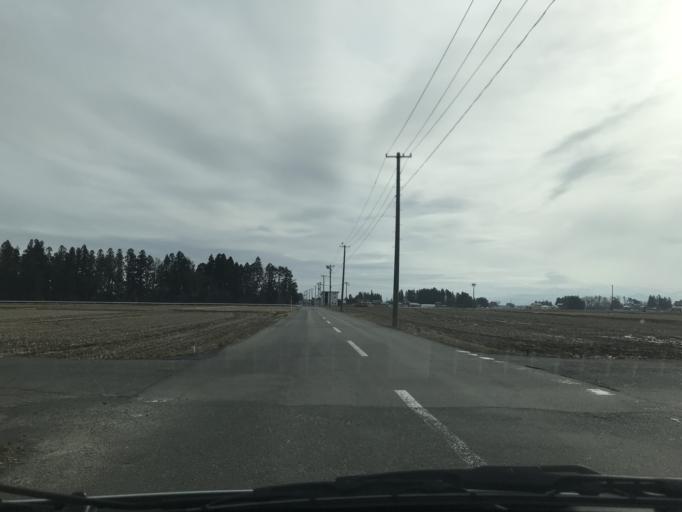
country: JP
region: Iwate
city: Hanamaki
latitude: 39.4045
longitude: 141.0764
